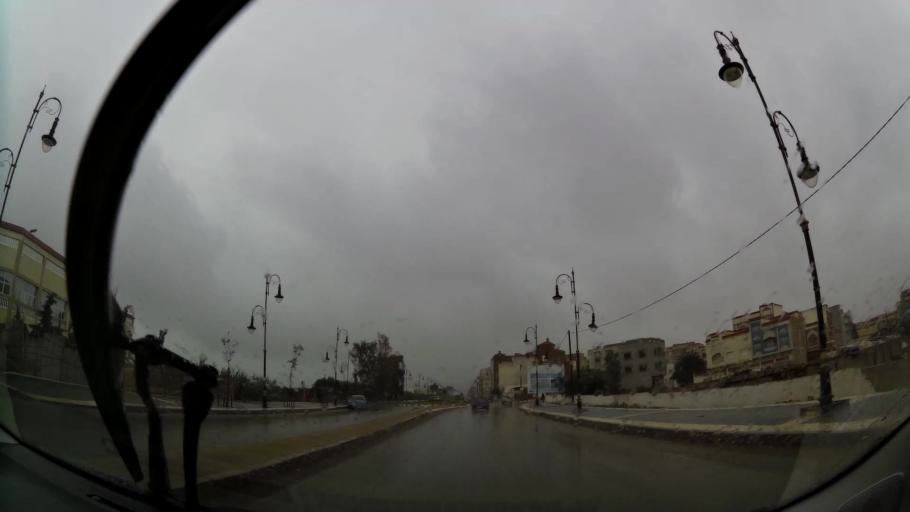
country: MA
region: Taza-Al Hoceima-Taounate
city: Imzourene
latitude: 35.1156
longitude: -3.8419
